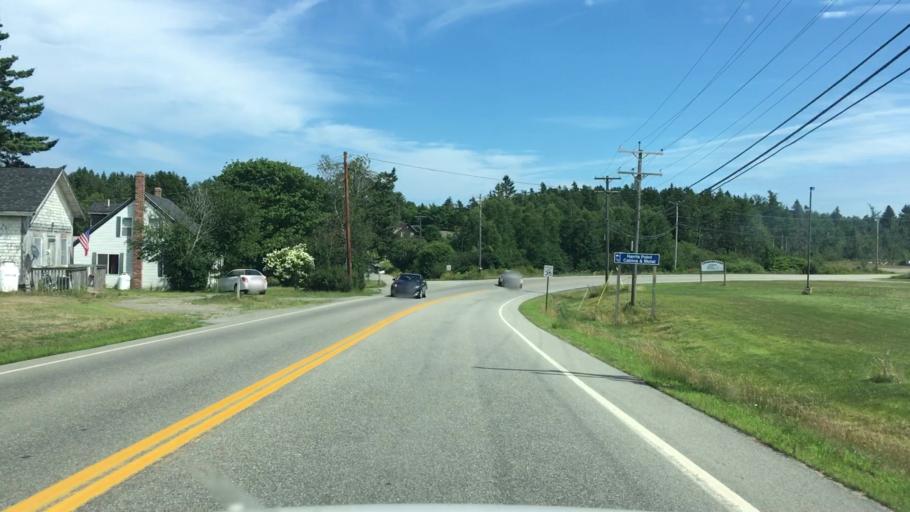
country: US
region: Maine
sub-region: Washington County
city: Eastport
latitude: 44.9127
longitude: -67.0019
